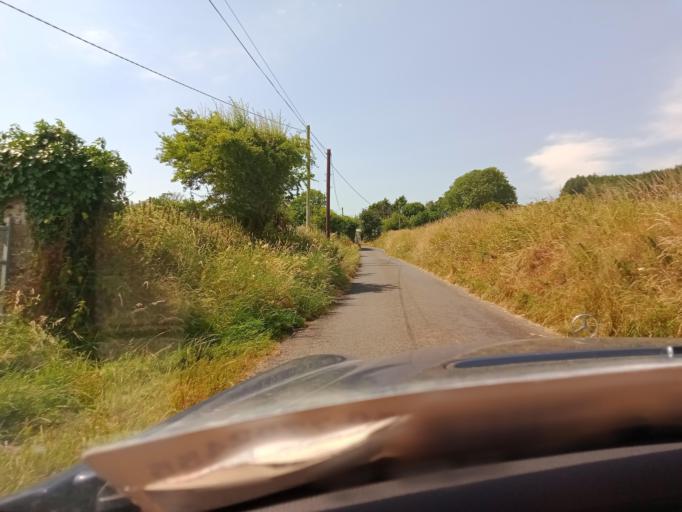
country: IE
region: Leinster
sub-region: Kilkenny
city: Mooncoin
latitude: 52.2564
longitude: -7.2064
